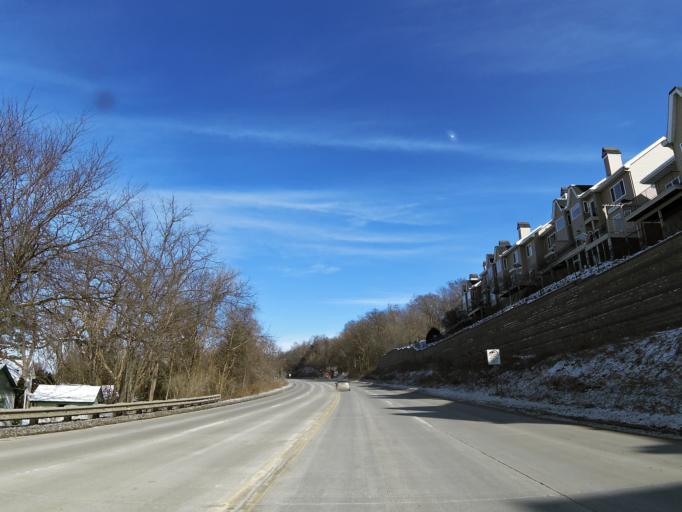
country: US
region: Wisconsin
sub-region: Pierce County
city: Prescott
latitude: 44.7528
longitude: -92.8032
